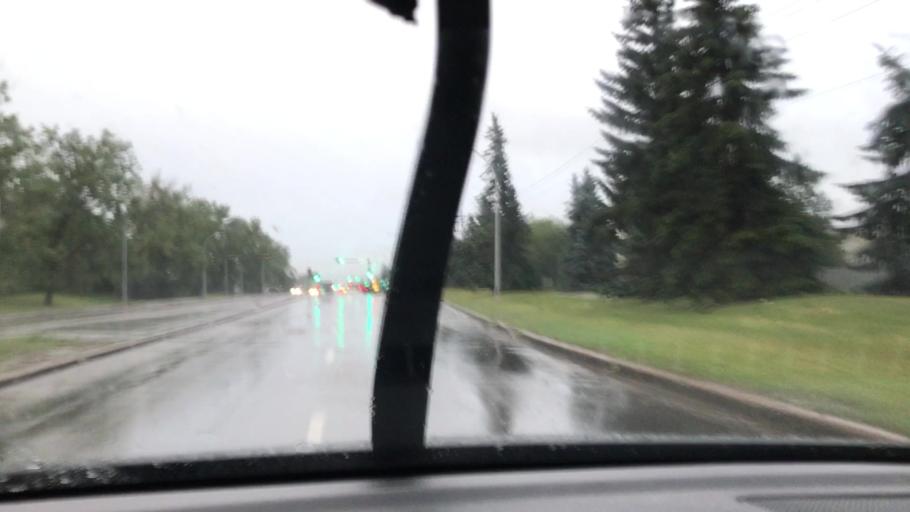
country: CA
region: Alberta
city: Sherwood Park
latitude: 53.5170
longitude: -113.3200
